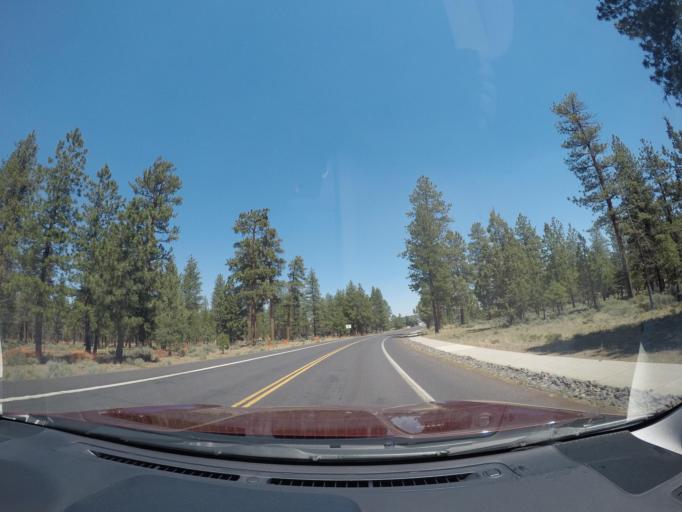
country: US
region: Oregon
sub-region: Deschutes County
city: Sisters
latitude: 44.2969
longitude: -121.5565
